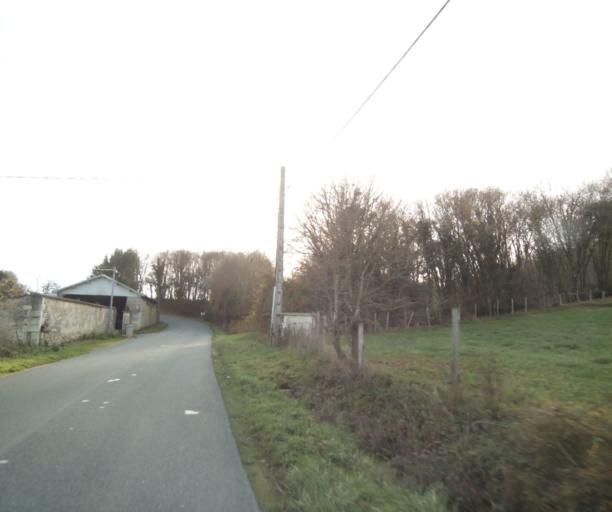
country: FR
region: Poitou-Charentes
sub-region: Departement de la Charente-Maritime
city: Chaniers
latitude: 45.7443
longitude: -0.5428
